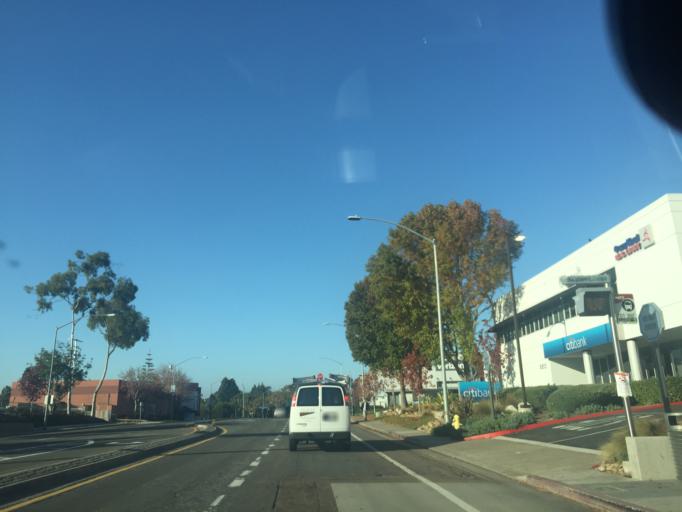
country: US
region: California
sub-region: San Diego County
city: La Jolla
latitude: 32.8681
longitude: -117.2316
